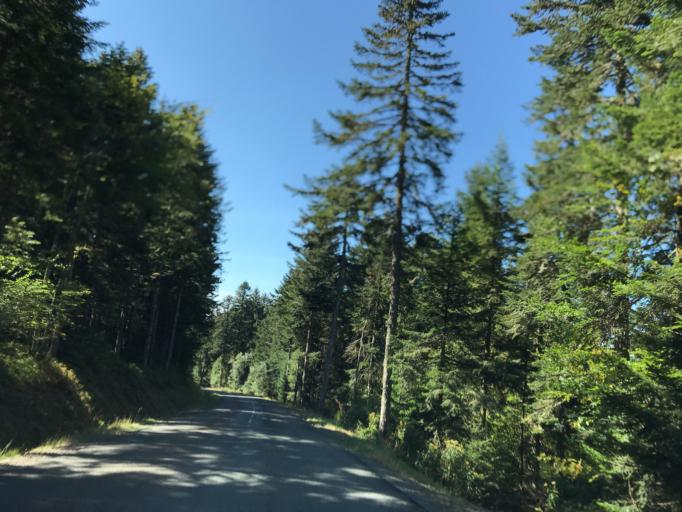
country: FR
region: Rhone-Alpes
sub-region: Departement de la Loire
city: Noiretable
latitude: 45.7607
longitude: 3.7714
